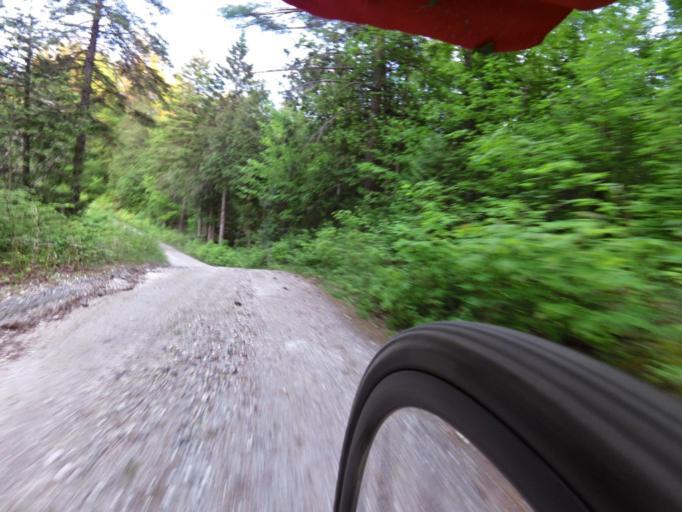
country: CA
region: Ontario
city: Arnprior
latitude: 45.1795
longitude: -76.5089
